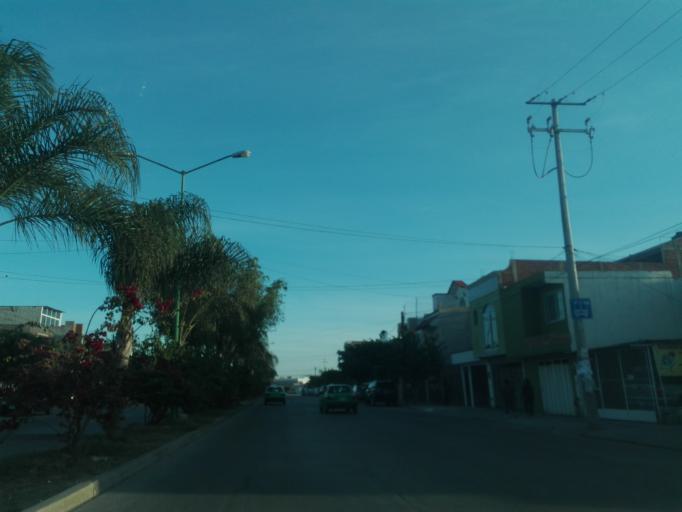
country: MX
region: Guanajuato
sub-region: Leon
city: San Jose de Duran (Los Troncoso)
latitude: 21.0798
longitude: -101.6394
